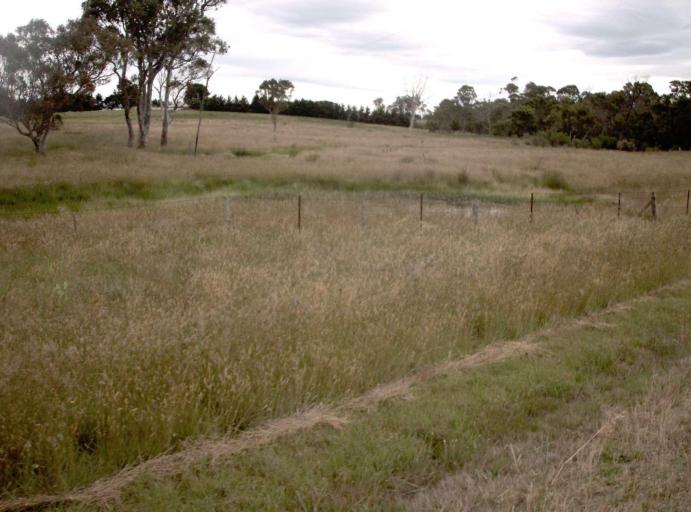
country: AU
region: Victoria
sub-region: East Gippsland
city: Bairnsdale
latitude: -37.9764
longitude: 147.4645
